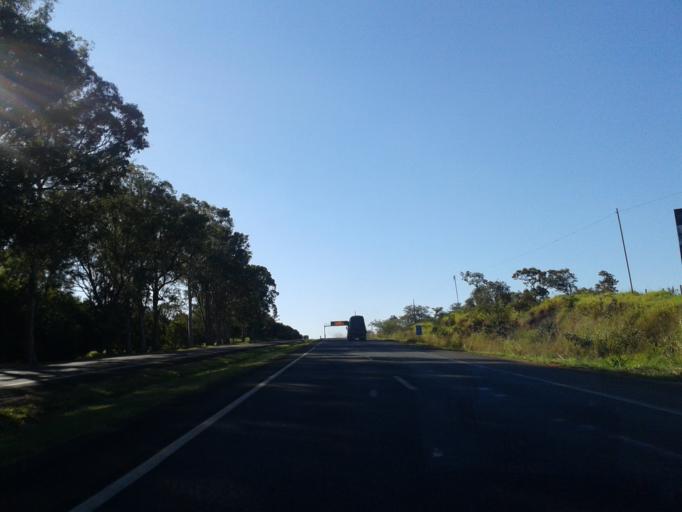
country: BR
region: Minas Gerais
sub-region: Uberlandia
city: Uberlandia
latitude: -18.9821
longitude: -48.2127
